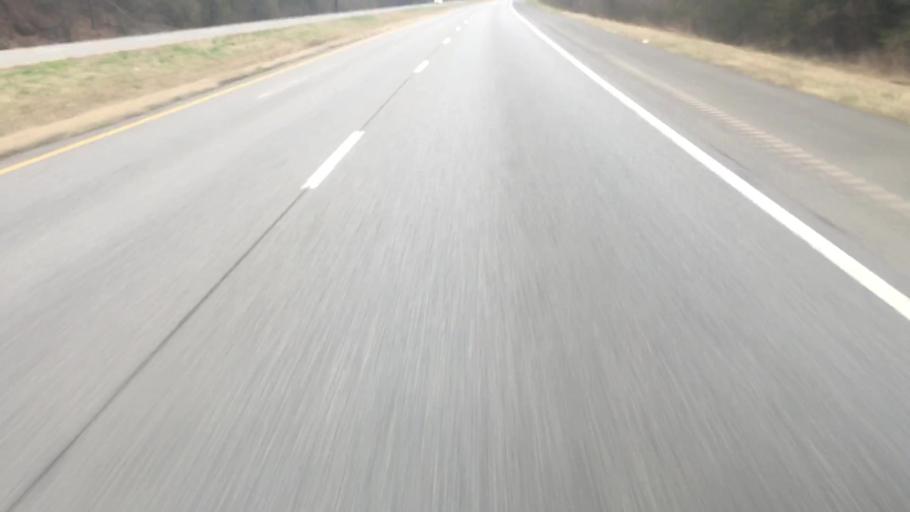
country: US
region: Alabama
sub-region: Jefferson County
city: Graysville
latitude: 33.6753
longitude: -86.9720
